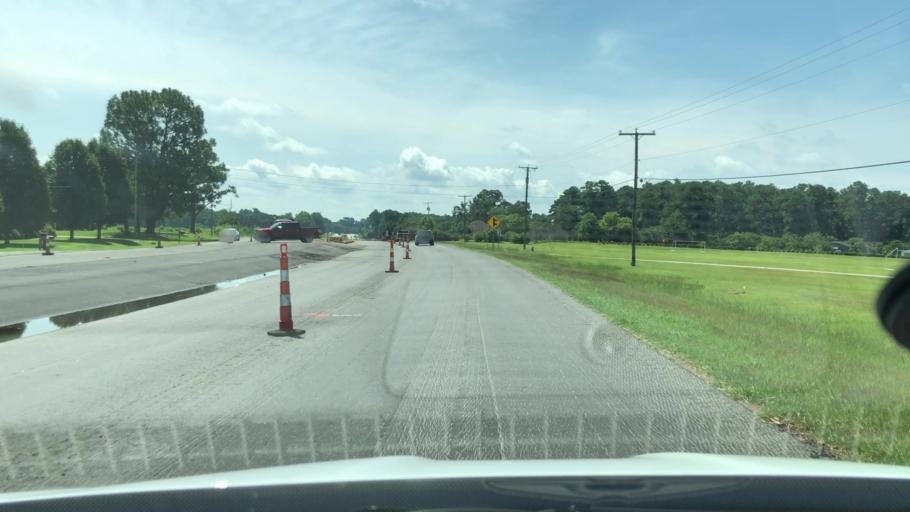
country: US
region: North Carolina
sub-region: Martin County
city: Williamston
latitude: 35.8147
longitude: -77.0648
